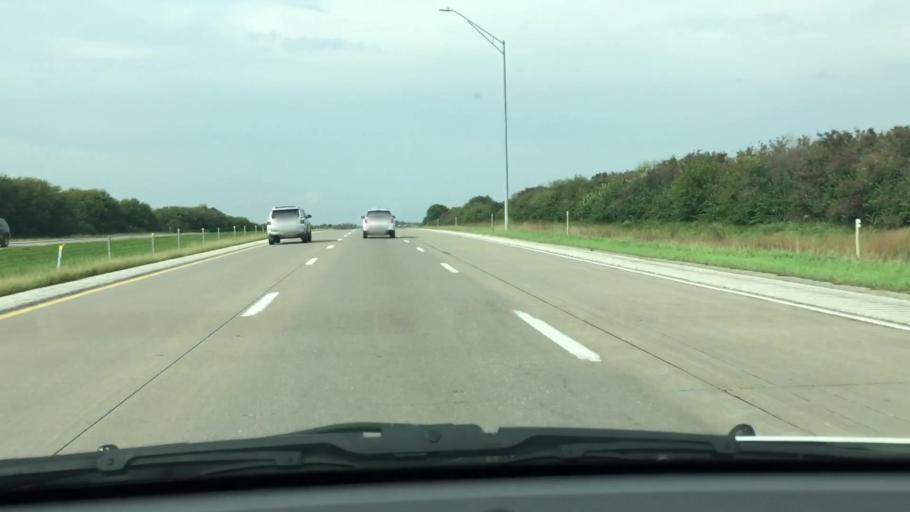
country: US
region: Iowa
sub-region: Cedar County
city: Durant
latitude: 41.6332
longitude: -90.8659
